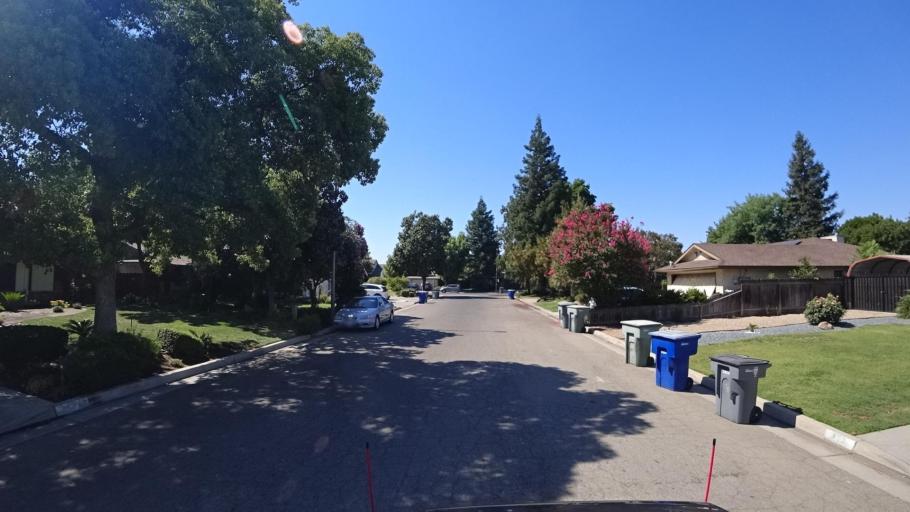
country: US
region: California
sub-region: Fresno County
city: Sunnyside
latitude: 36.7492
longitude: -119.6892
